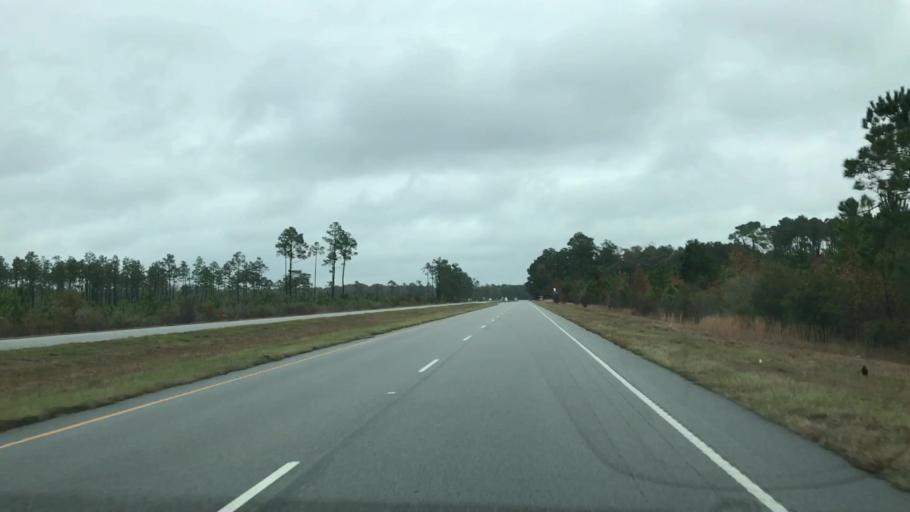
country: US
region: South Carolina
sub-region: Charleston County
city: Awendaw
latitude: 33.1709
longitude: -79.4191
